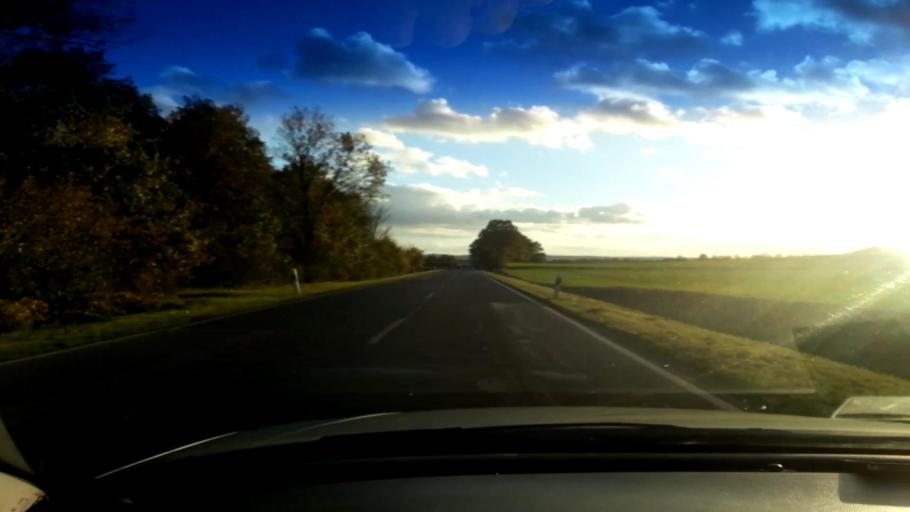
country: DE
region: Bavaria
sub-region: Upper Franconia
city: Zapfendorf
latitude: 50.0347
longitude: 10.9145
